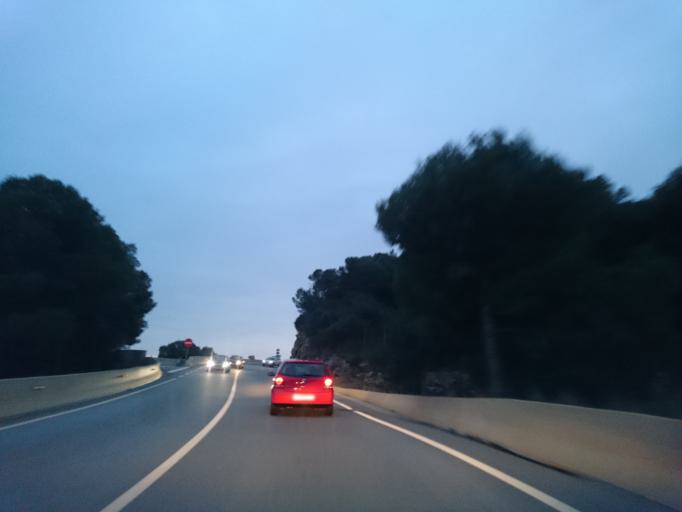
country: ES
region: Catalonia
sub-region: Provincia de Barcelona
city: Castelldefels
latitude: 41.2606
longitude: 1.9202
